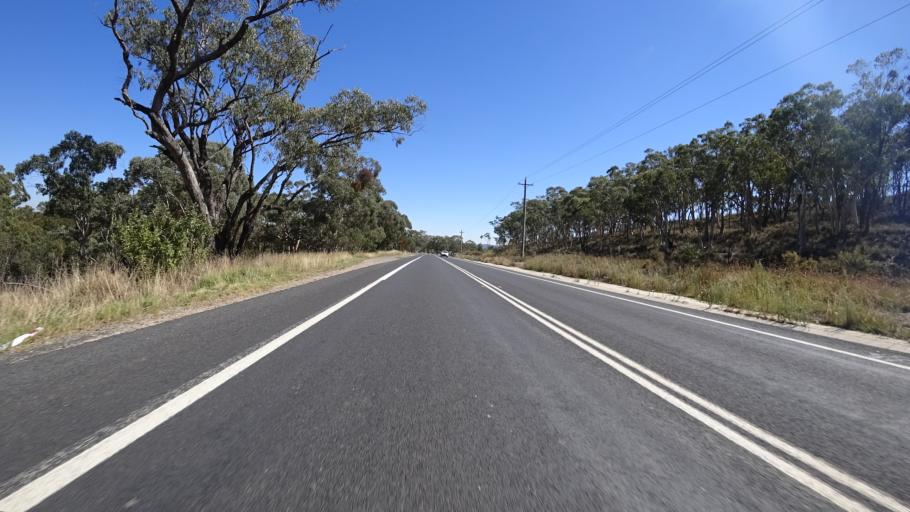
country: AU
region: New South Wales
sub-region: Lithgow
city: Lithgow
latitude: -33.4224
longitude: 150.1034
